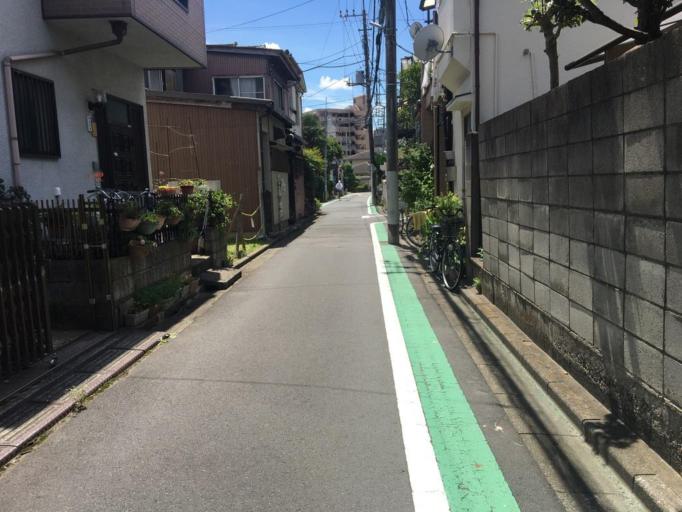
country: JP
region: Chiba
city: Matsudo
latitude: 35.7407
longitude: 139.8587
